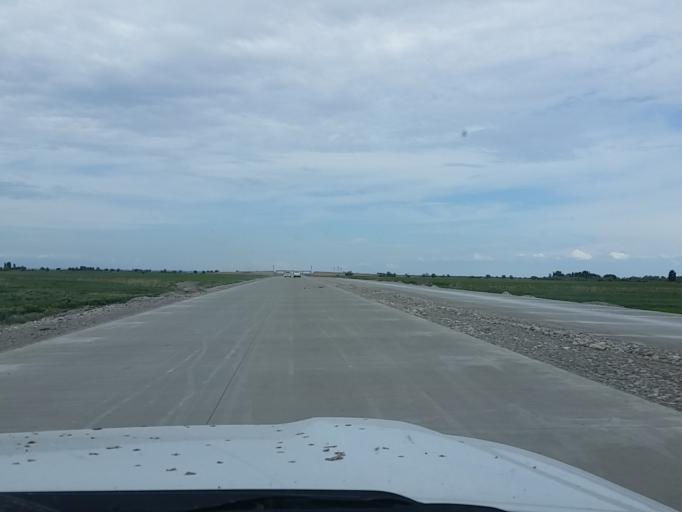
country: KZ
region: Almaty Oblysy
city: Zharkent
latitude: 44.0286
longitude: 79.8873
